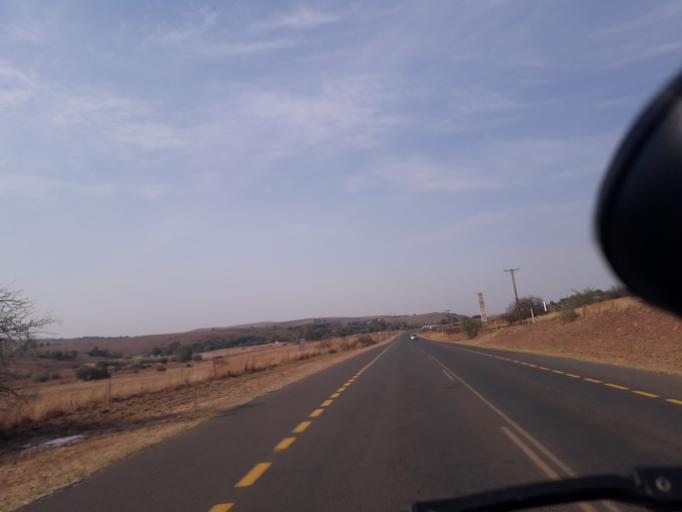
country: ZA
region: Gauteng
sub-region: West Rand District Municipality
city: Krugersdorp
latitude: -26.0190
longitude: 27.7275
